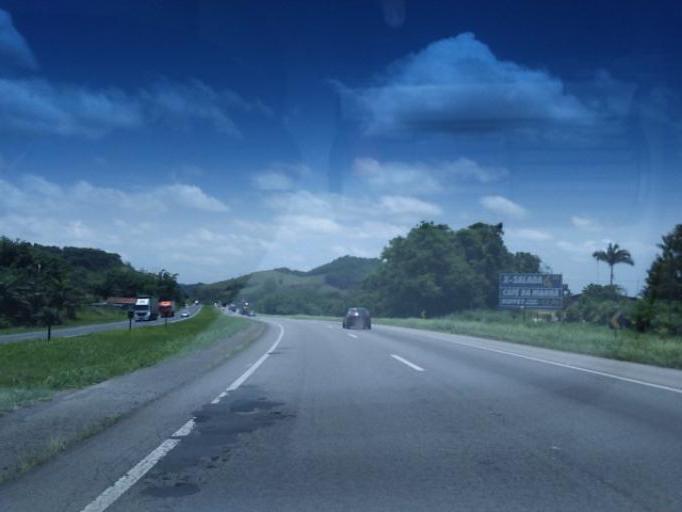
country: BR
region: Sao Paulo
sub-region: Juquia
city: Juquia
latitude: -24.3577
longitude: -47.6859
